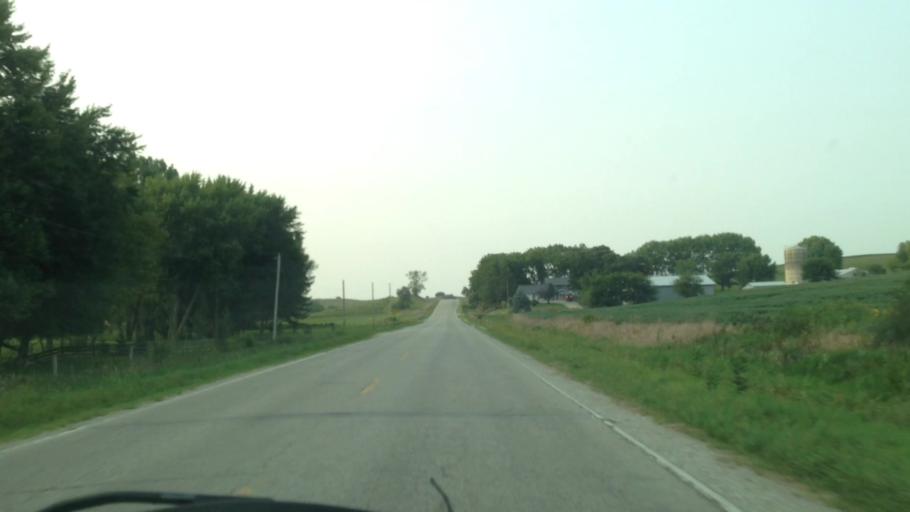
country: US
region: Iowa
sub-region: Iowa County
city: Marengo
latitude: 41.8751
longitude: -92.0890
